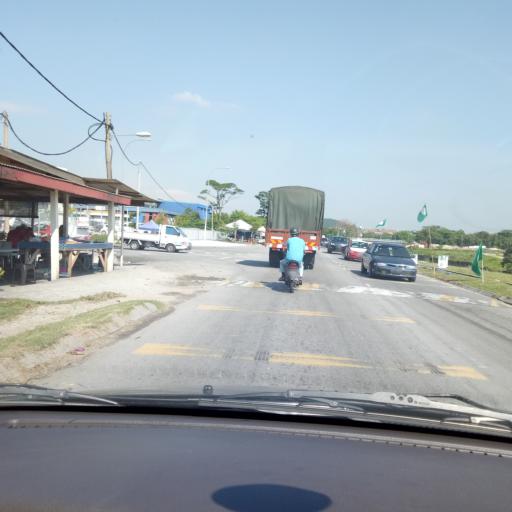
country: MY
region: Selangor
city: Kampong Baharu Balakong
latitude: 3.0153
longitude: 101.7663
